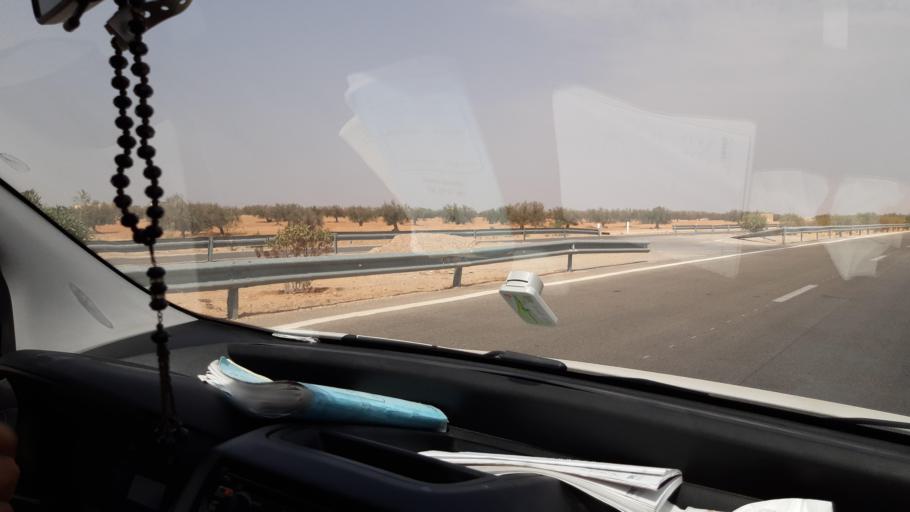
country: TN
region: Safaqis
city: Bi'r `Ali Bin Khalifah
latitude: 34.5640
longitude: 10.3463
